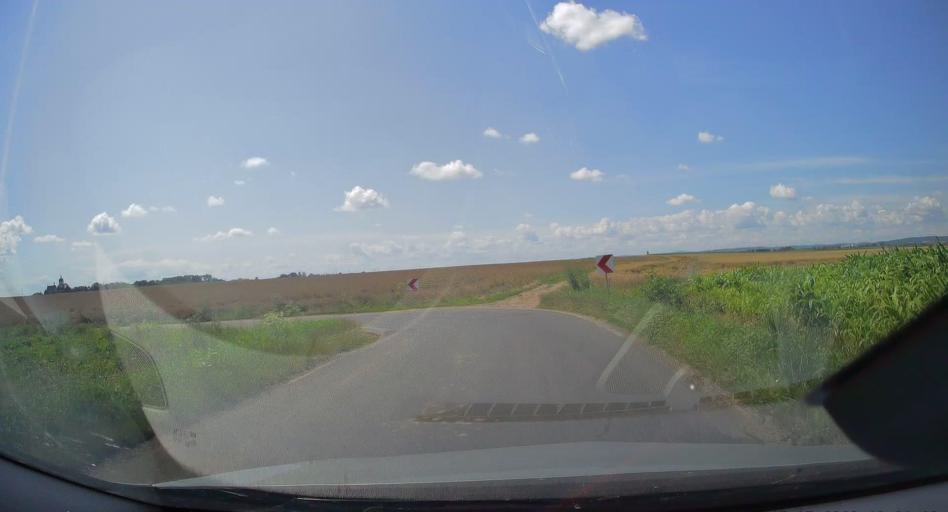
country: PL
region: Subcarpathian Voivodeship
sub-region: Powiat jaroslawski
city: Sosnica
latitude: 49.8502
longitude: 22.8772
